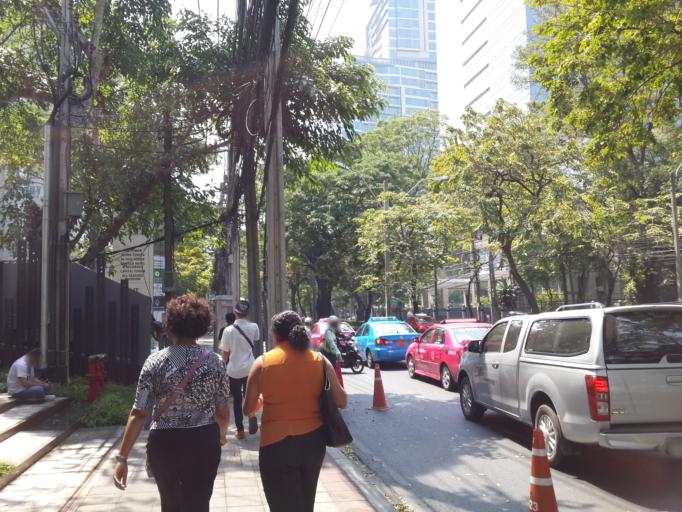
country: TH
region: Bangkok
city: Ratchathewi
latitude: 13.7401
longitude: 100.5470
